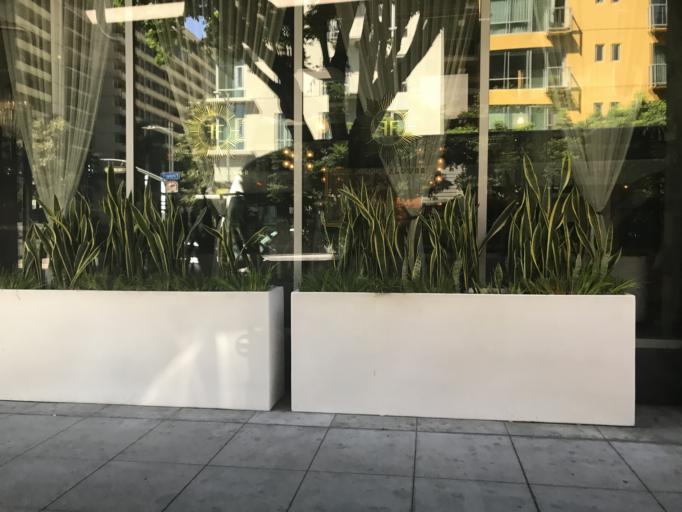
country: US
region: California
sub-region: Los Angeles County
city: Los Angeles
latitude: 34.0460
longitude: -118.2612
